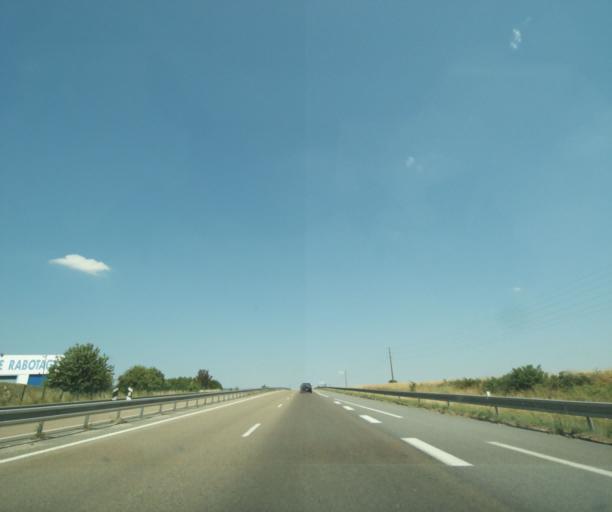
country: FR
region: Champagne-Ardenne
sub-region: Departement de la Marne
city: Chalons-en-Champagne
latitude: 48.9863
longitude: 4.3493
